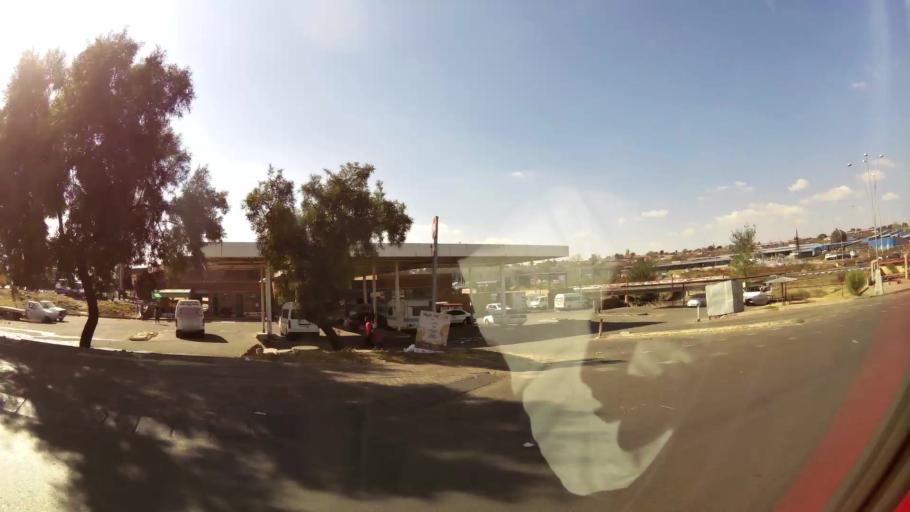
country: ZA
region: Gauteng
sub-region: City of Johannesburg Metropolitan Municipality
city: Soweto
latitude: -26.2395
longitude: 27.9119
